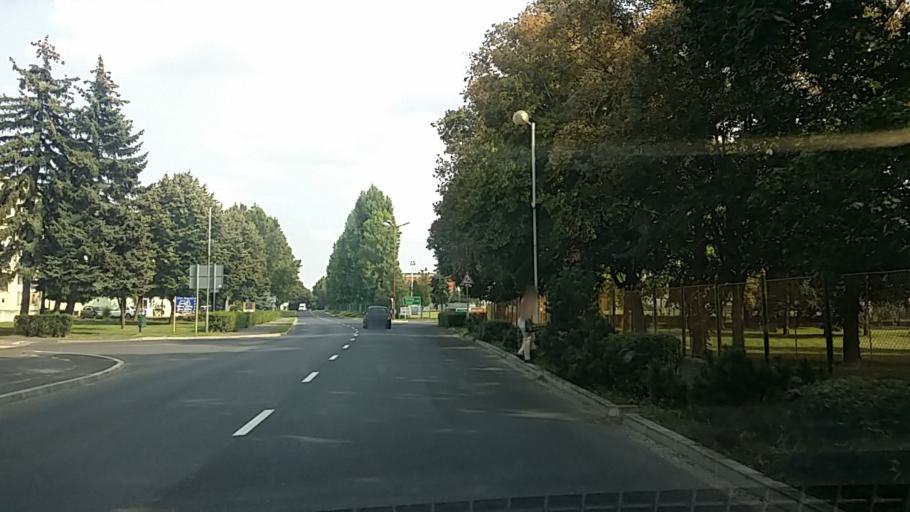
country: HU
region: Komarom-Esztergom
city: Babolna
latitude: 47.6405
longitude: 17.9829
